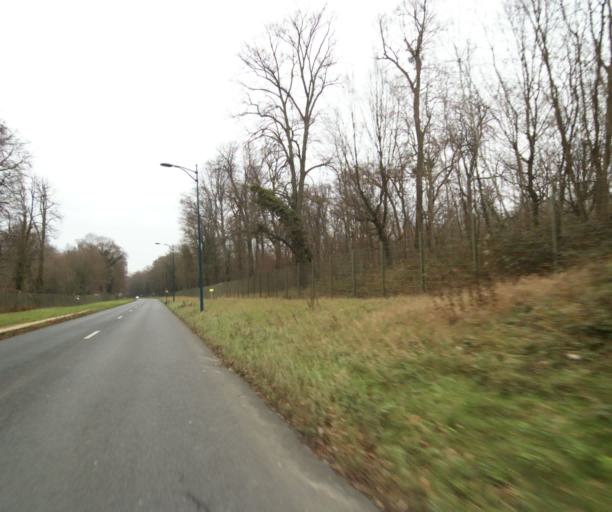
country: FR
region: Ile-de-France
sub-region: Departement des Hauts-de-Seine
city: Ville-d'Avray
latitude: 48.8331
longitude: 2.1987
